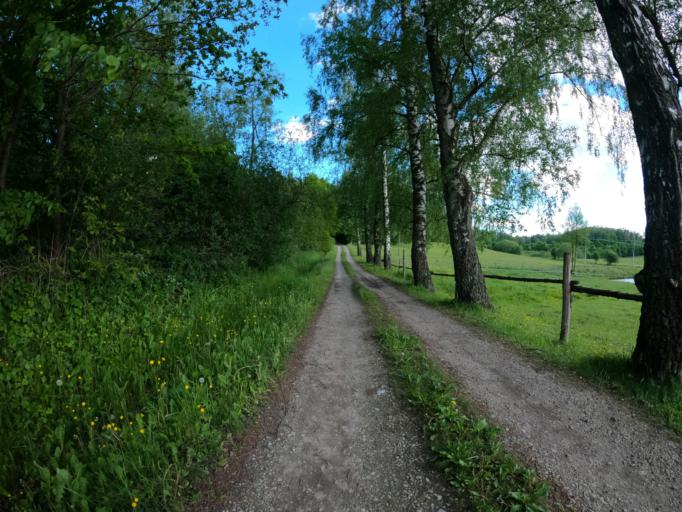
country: PL
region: Warmian-Masurian Voivodeship
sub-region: Powiat lidzbarski
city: Lidzbark Warminski
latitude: 54.1288
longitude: 20.6074
